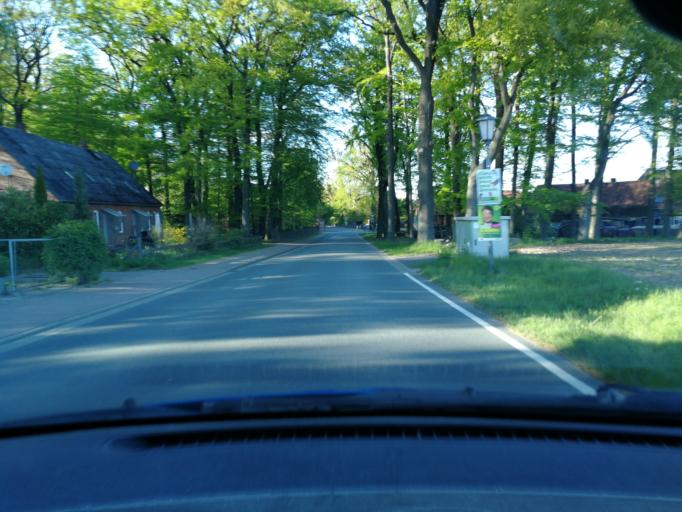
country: DE
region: Lower Saxony
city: Betzendorf
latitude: 53.1083
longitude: 10.3010
